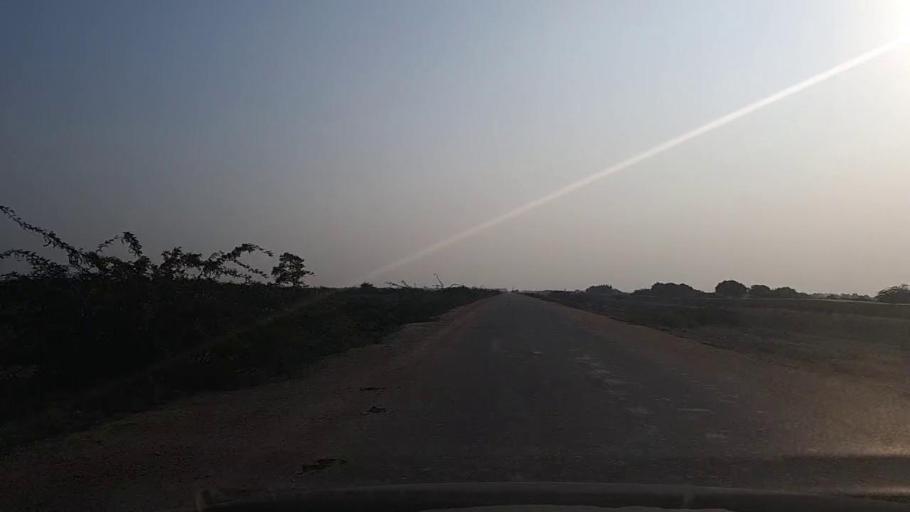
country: PK
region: Sindh
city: Mirpur Sakro
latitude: 24.4821
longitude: 67.8055
